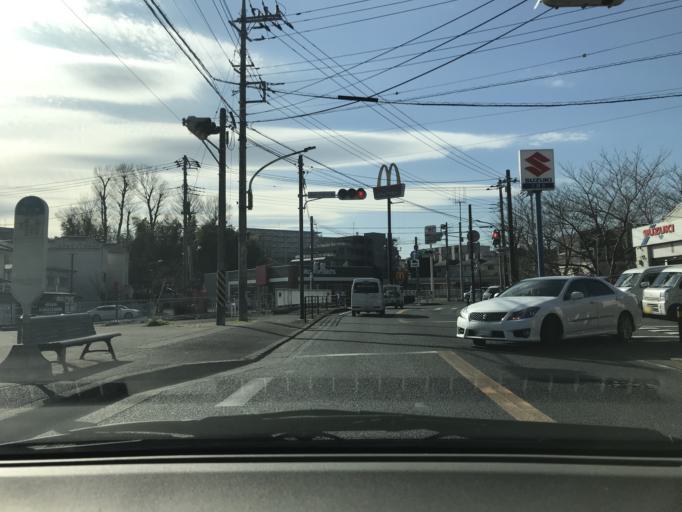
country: JP
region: Tokyo
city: Chofugaoka
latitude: 35.5975
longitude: 139.5624
